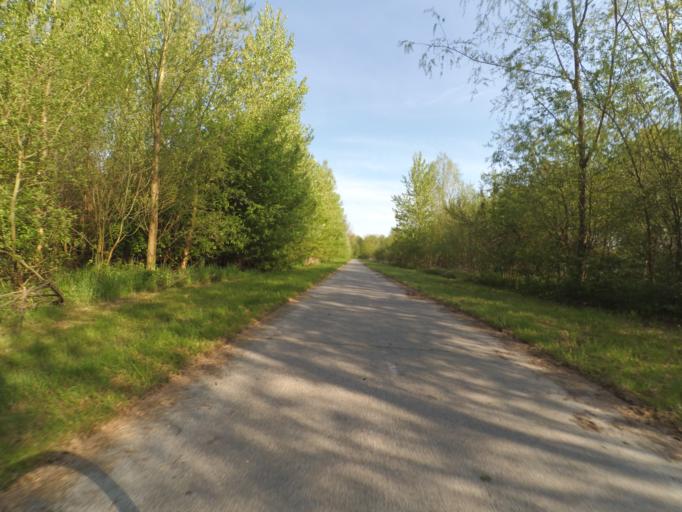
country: NL
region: North Holland
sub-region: Gemeente Huizen
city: Huizen
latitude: 52.3399
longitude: 5.2943
